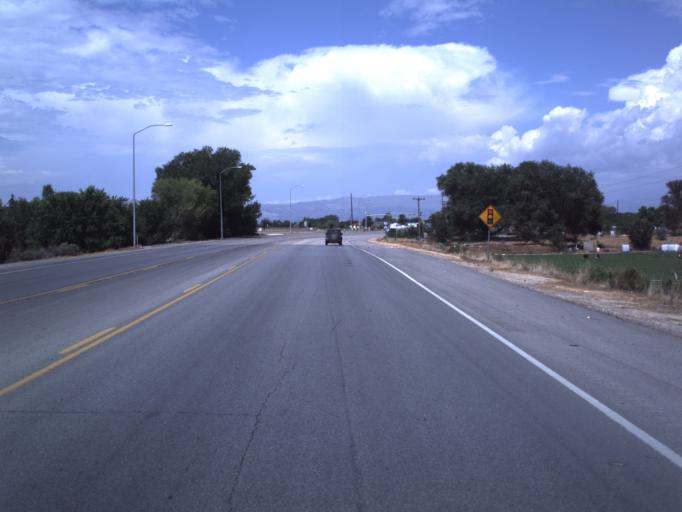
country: US
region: Utah
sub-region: Uintah County
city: Naples
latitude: 40.4126
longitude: -109.4950
